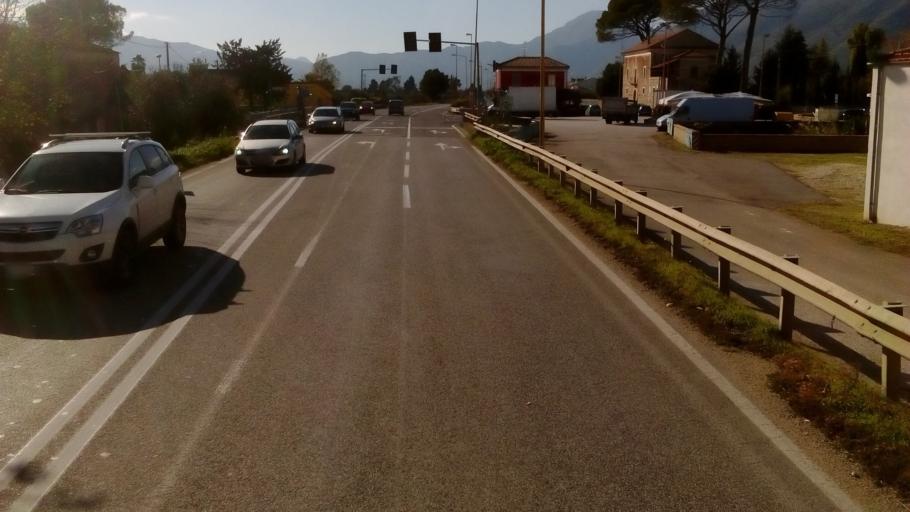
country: IT
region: Molise
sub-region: Provincia di Isernia
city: Taverna Ravindola
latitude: 41.5029
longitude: 14.1010
